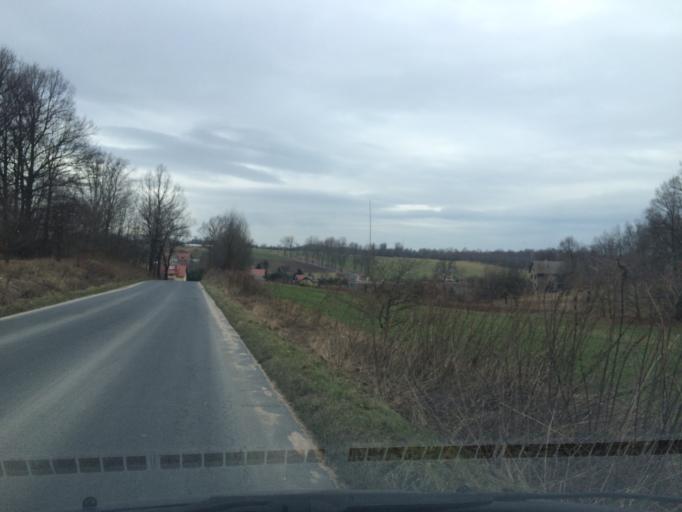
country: PL
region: Lower Silesian Voivodeship
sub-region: Powiat lwowecki
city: Lwowek Slaski
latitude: 51.1227
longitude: 15.4964
